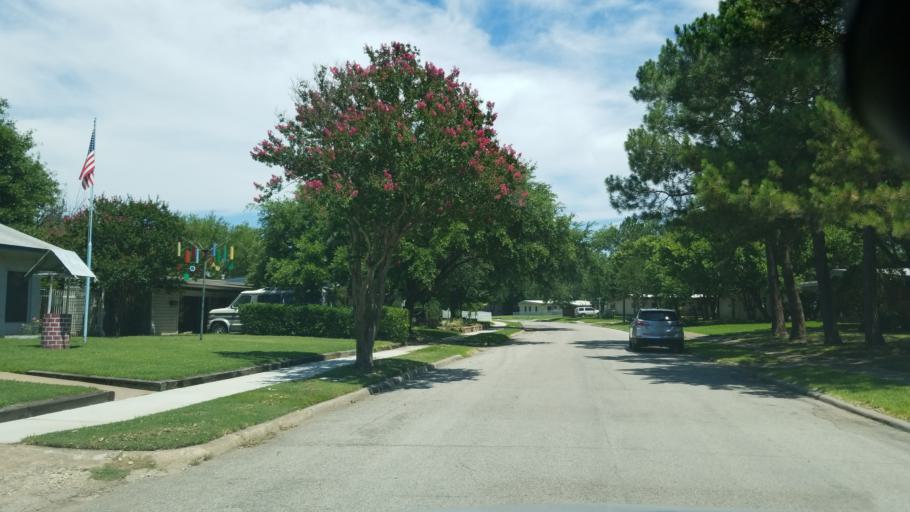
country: US
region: Texas
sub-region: Dallas County
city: Irving
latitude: 32.8326
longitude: -96.9700
